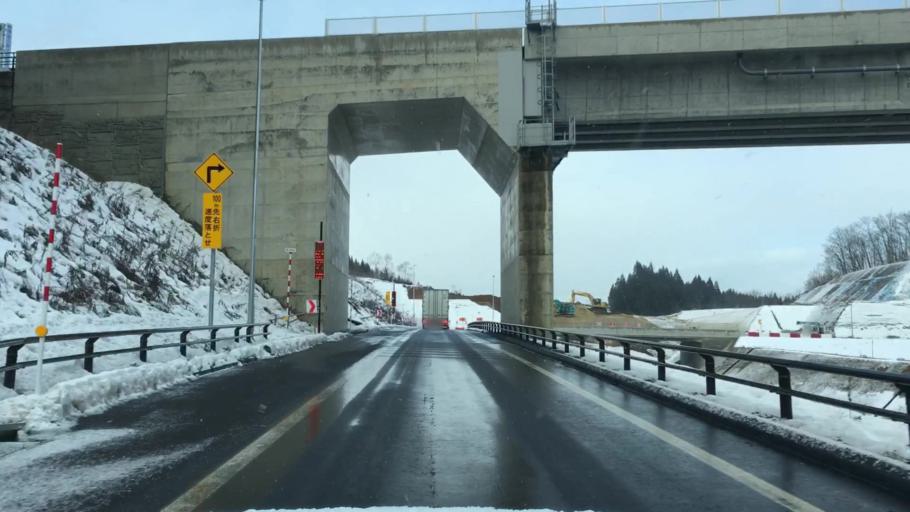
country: JP
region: Akita
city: Takanosu
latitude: 40.1985
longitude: 140.3748
